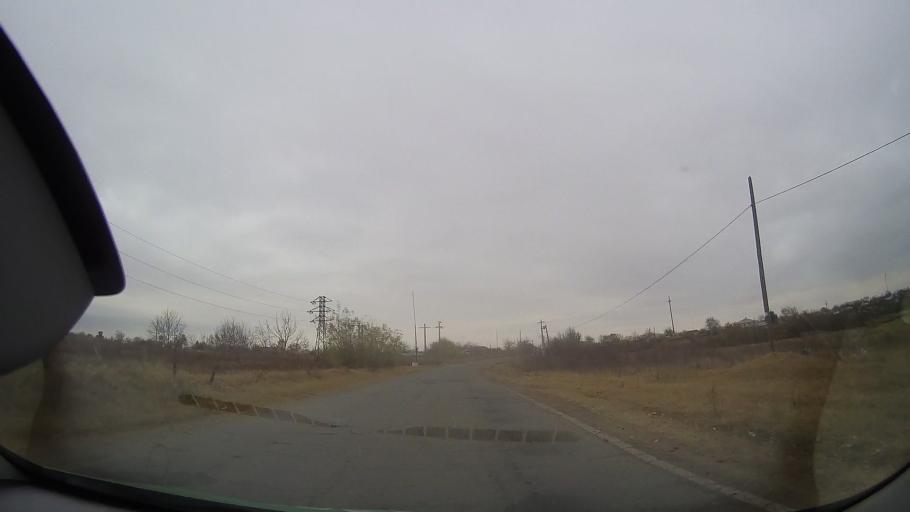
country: RO
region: Buzau
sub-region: Comuna Rusetu
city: Rusetu
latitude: 44.9529
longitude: 27.2194
